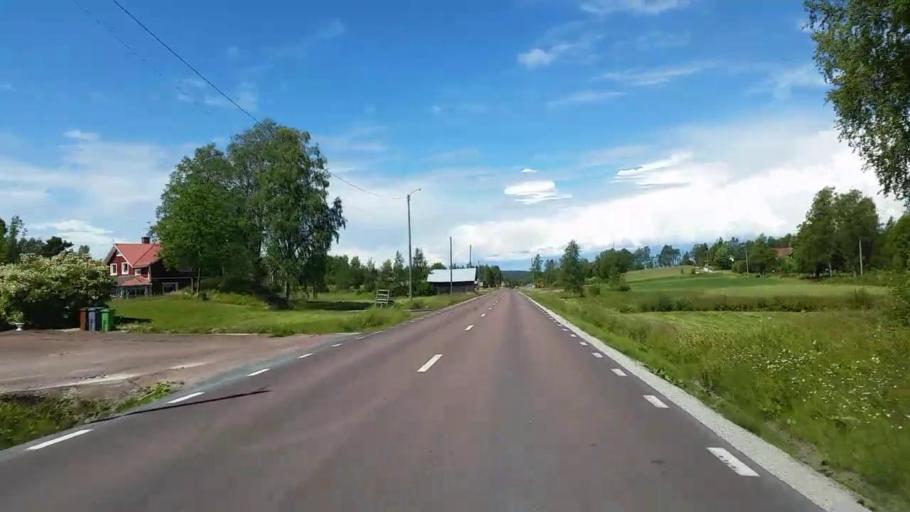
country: SE
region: Dalarna
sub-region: Rattviks Kommun
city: Raettvik
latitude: 61.0375
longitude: 15.2000
